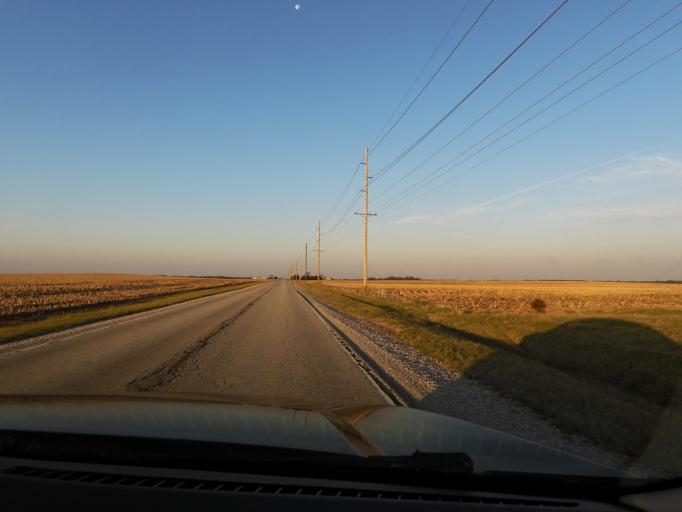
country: US
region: Illinois
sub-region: Marion County
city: Odin
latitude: 38.7651
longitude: -89.0149
